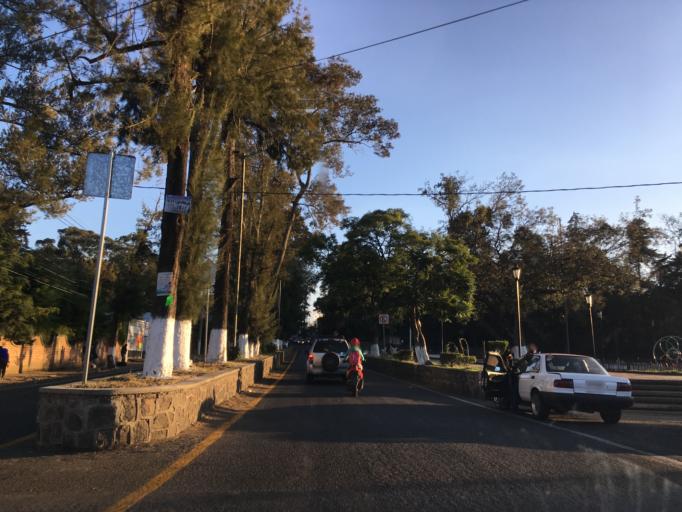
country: MX
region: Michoacan
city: Patzcuaro
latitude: 19.5393
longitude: -101.6120
